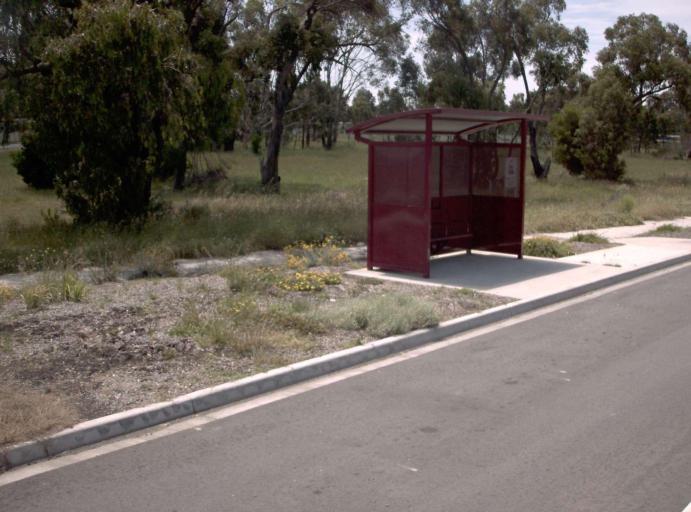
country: AU
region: Victoria
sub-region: Latrobe
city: Traralgon
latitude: -38.2176
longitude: 146.4762
